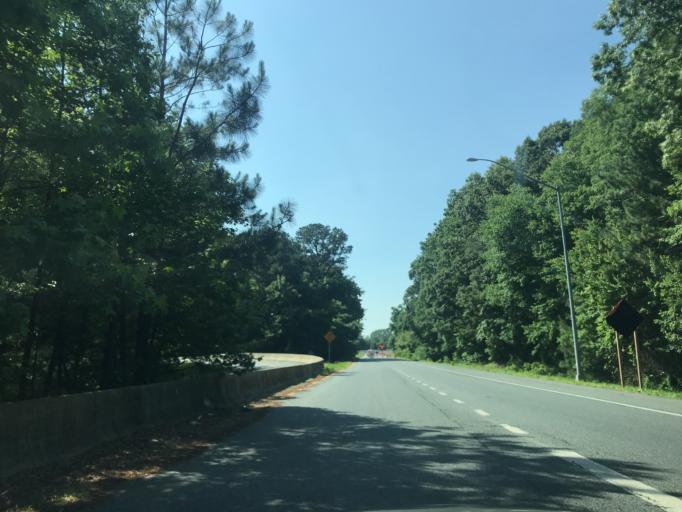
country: US
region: Maryland
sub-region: Wicomico County
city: Salisbury
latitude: 38.3711
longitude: -75.5355
